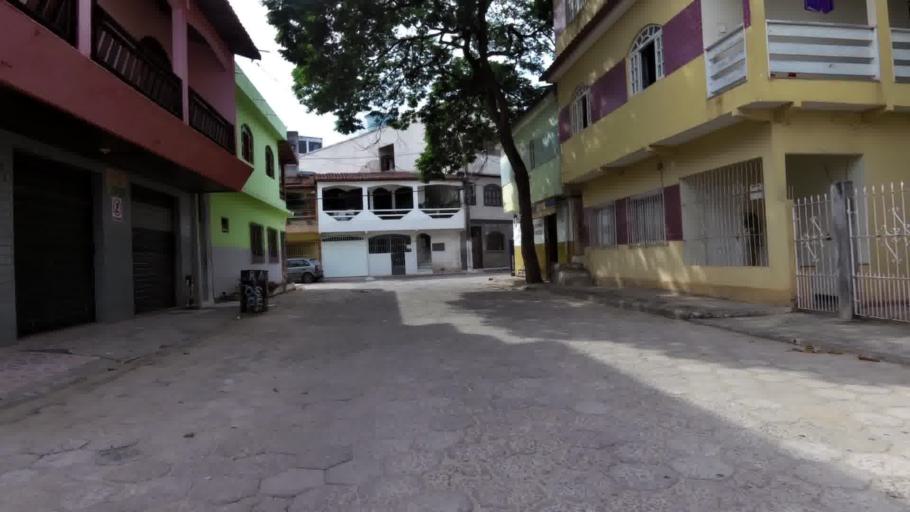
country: BR
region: Espirito Santo
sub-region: Piuma
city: Piuma
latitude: -20.8400
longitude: -40.7261
